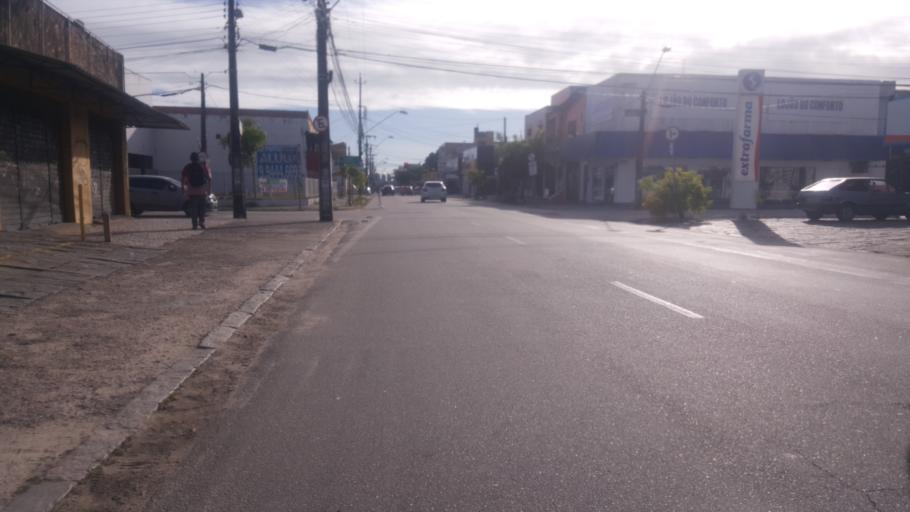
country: BR
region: Ceara
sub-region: Fortaleza
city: Fortaleza
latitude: -3.7678
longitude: -38.5514
